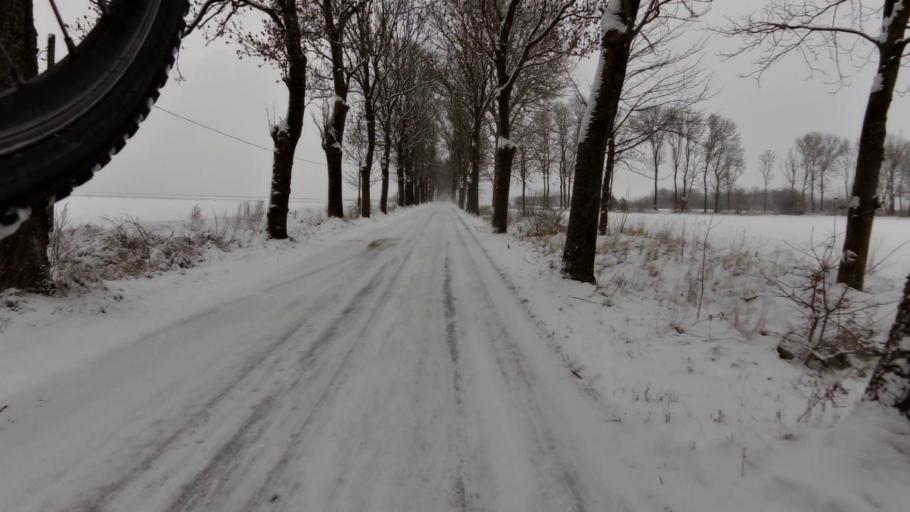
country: PL
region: West Pomeranian Voivodeship
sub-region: Powiat bialogardzki
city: Bialogard
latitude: 53.9574
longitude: 15.9689
